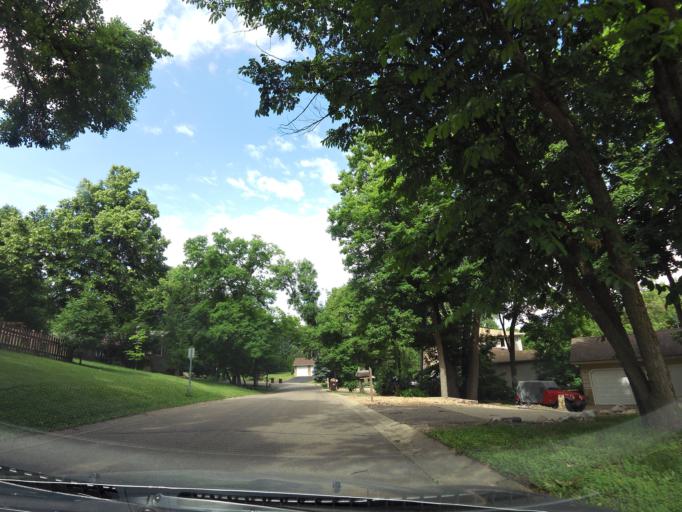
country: US
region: Minnesota
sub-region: Scott County
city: Prior Lake
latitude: 44.7058
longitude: -93.4516
